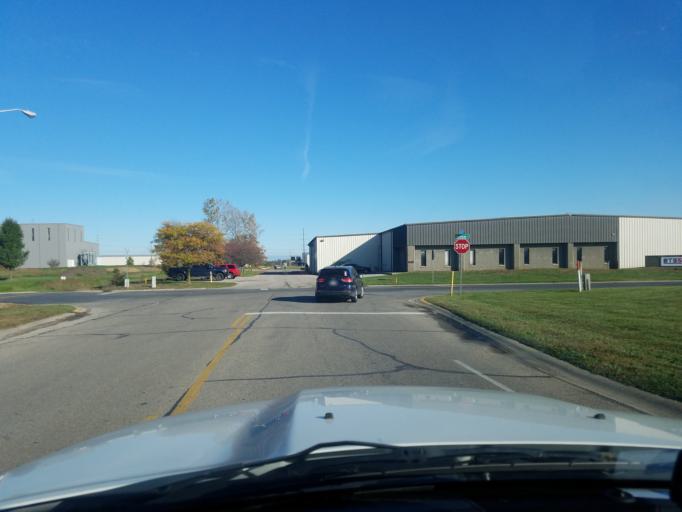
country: US
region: Indiana
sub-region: Jackson County
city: Seymour
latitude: 38.9691
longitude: -85.8622
